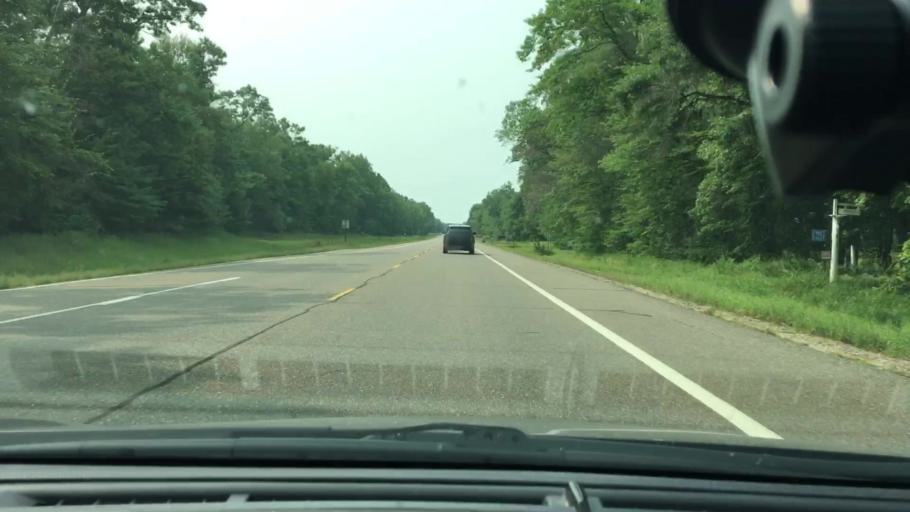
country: US
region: Minnesota
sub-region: Crow Wing County
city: Breezy Point
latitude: 46.5095
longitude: -94.1359
